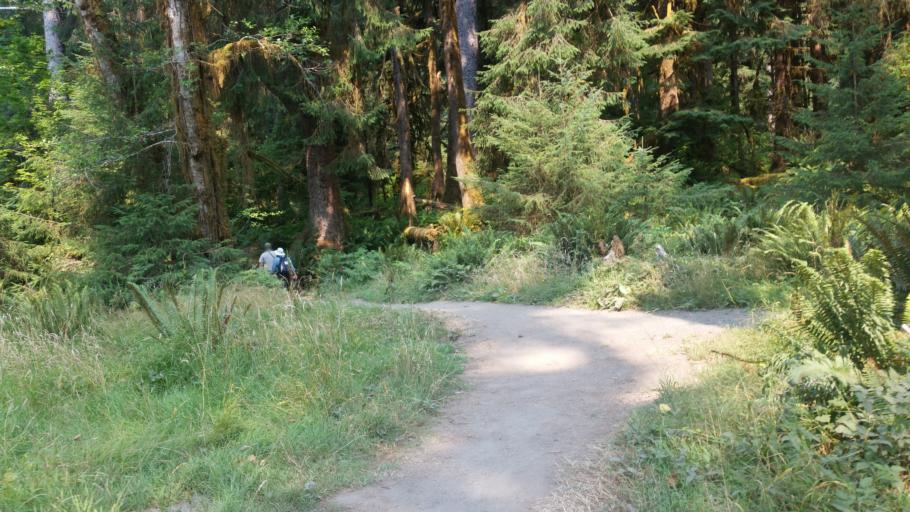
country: US
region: Washington
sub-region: Clallam County
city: Forks
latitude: 47.8593
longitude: -123.9265
